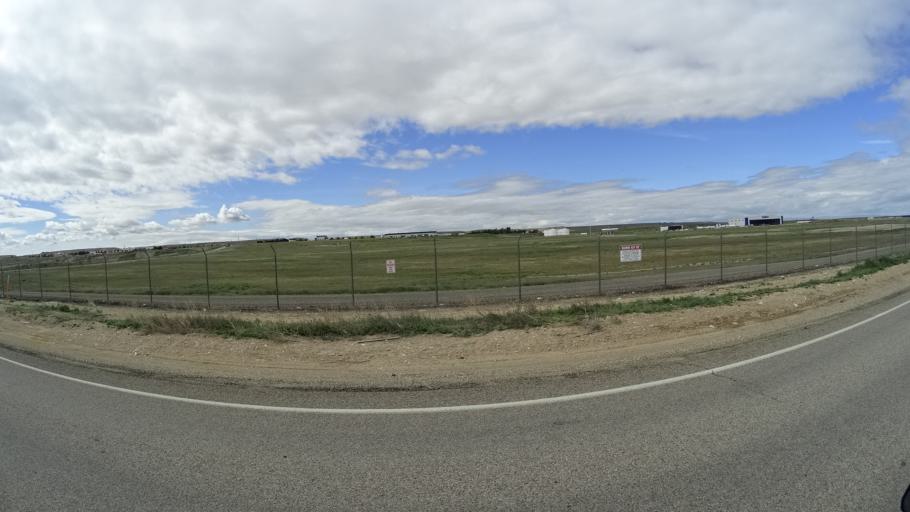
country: US
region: Idaho
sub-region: Ada County
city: Boise
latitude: 43.5553
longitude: -116.1888
